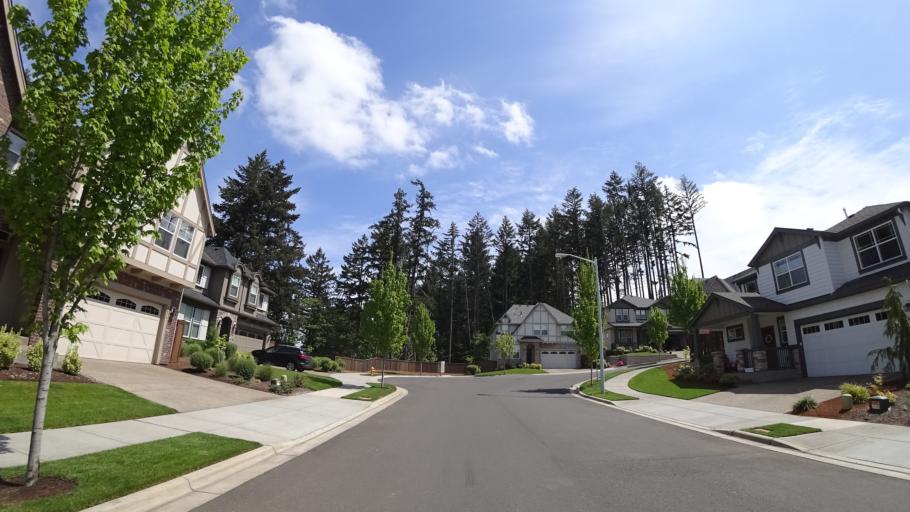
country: US
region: Oregon
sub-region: Washington County
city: Aloha
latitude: 45.4648
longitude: -122.8872
